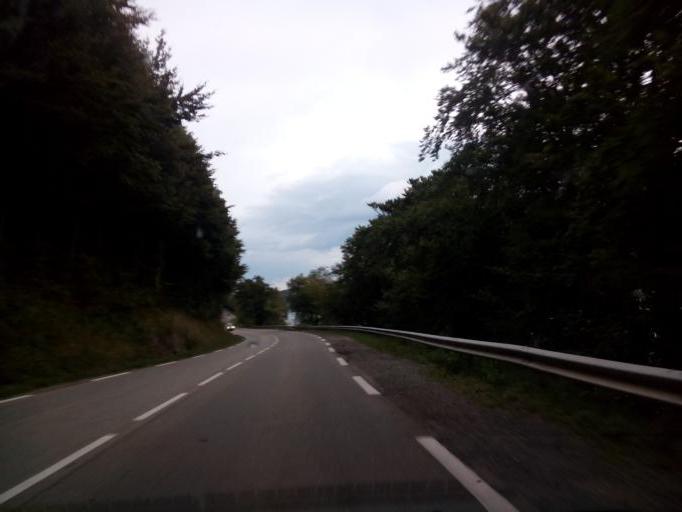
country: FR
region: Rhone-Alpes
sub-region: Departement de l'Isere
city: Pierre-Chatel
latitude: 45.0027
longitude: 5.7721
